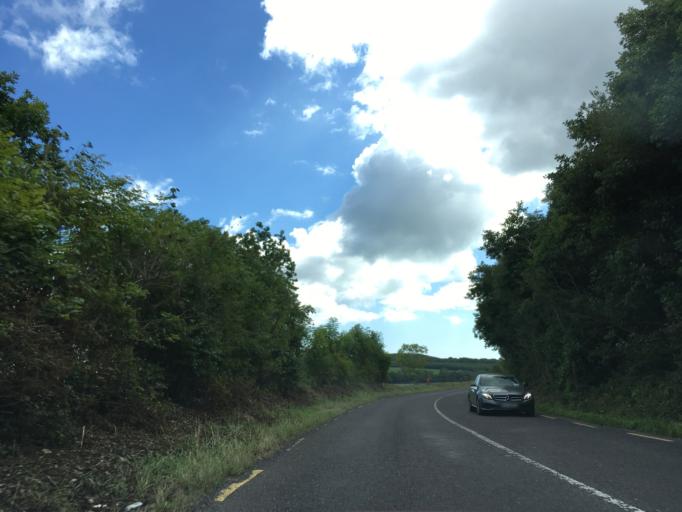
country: IE
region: Munster
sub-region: County Cork
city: Carrigaline
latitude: 51.8097
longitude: -8.3511
